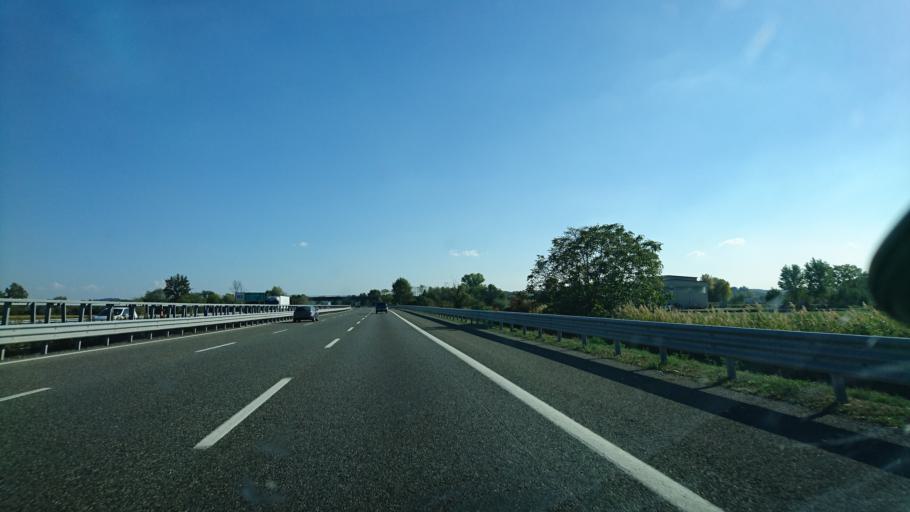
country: IT
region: Piedmont
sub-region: Provincia di Alessandria
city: Occimiano
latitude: 45.0619
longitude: 8.5139
